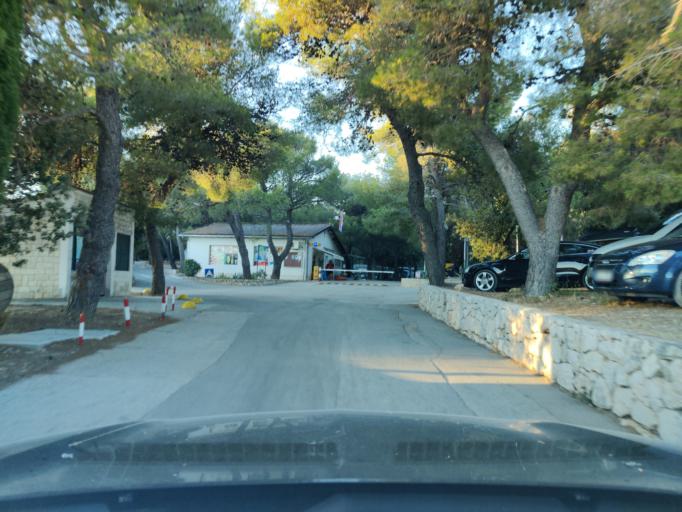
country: HR
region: Sibensko-Kniniska
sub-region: Grad Sibenik
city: Tisno
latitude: 43.8088
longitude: 15.6285
